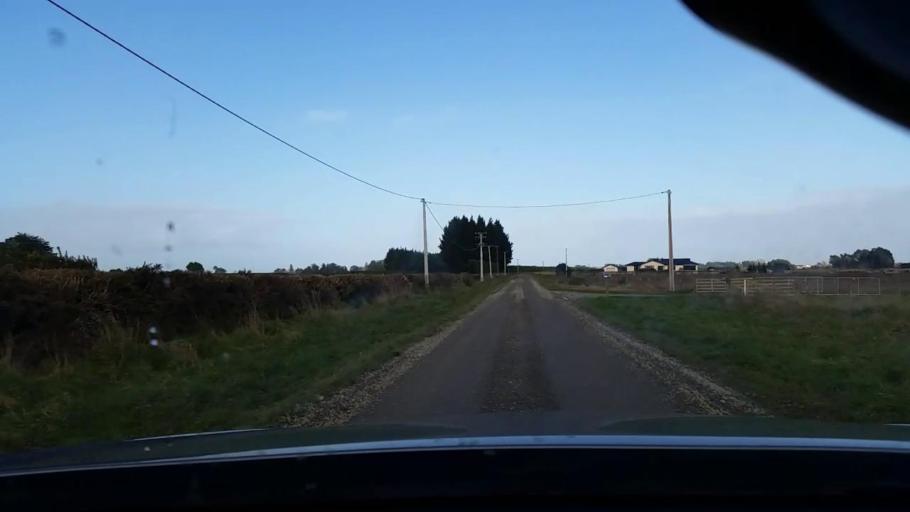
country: NZ
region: Southland
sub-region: Invercargill City
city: Invercargill
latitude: -46.2790
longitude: 168.2936
